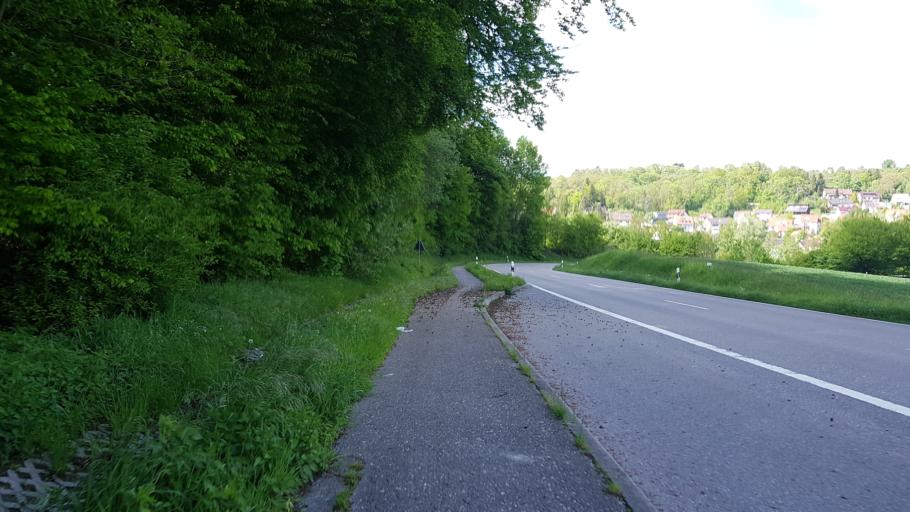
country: DE
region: Baden-Wuerttemberg
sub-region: Regierungsbezirk Stuttgart
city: Kirchberg an der Murr
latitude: 48.9371
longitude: 9.3308
